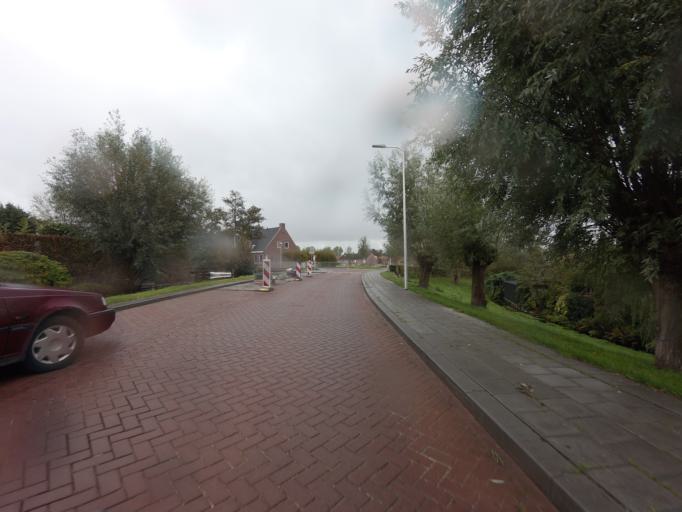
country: NL
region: South Holland
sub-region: Gemeente Rijnwoude
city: Benthuizen
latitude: 52.0959
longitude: 4.5865
